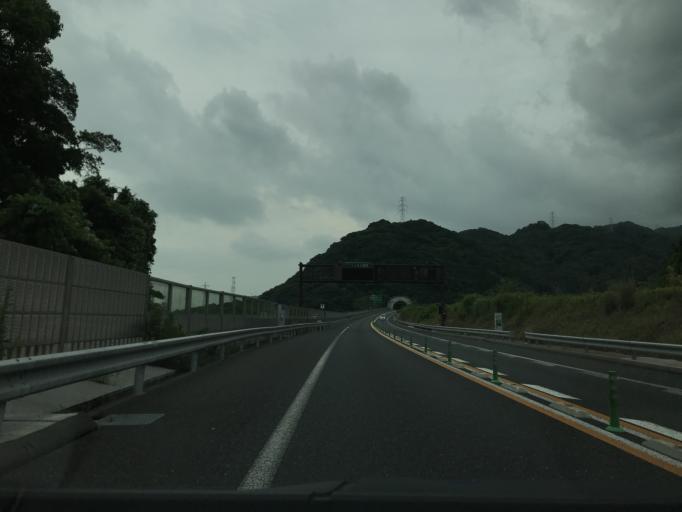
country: JP
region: Fukuoka
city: Kanda
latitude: 33.7809
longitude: 130.9713
